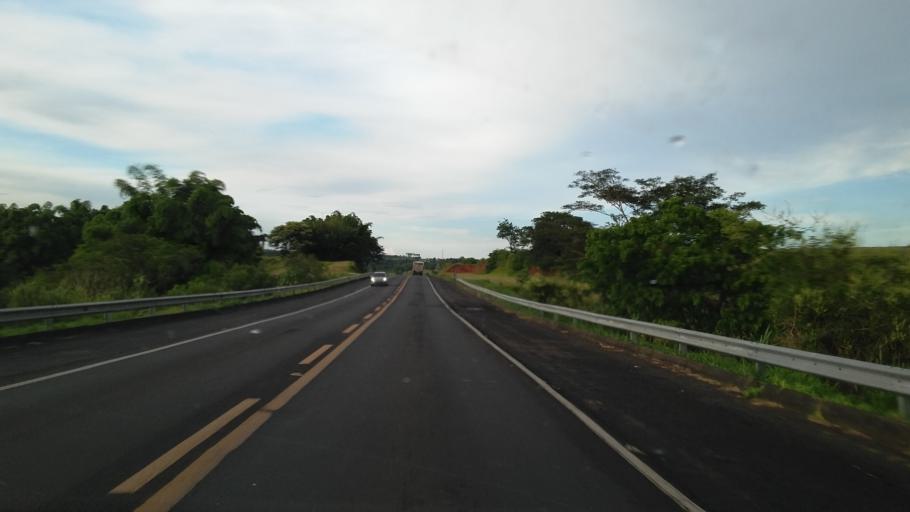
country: BR
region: Sao Paulo
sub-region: Marilia
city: Marilia
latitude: -21.9407
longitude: -49.9203
